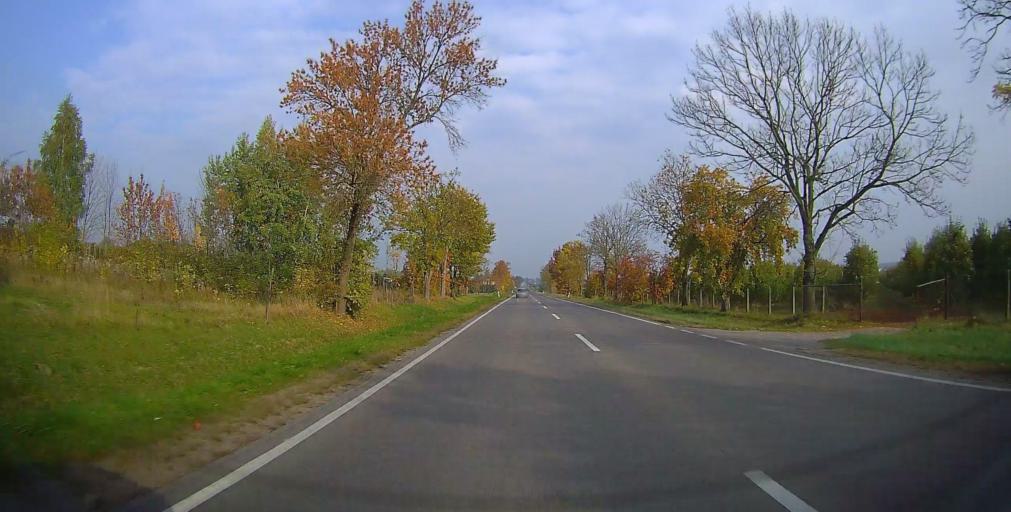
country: PL
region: Masovian Voivodeship
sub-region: Powiat grojecki
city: Bledow
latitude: 51.7544
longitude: 20.7651
